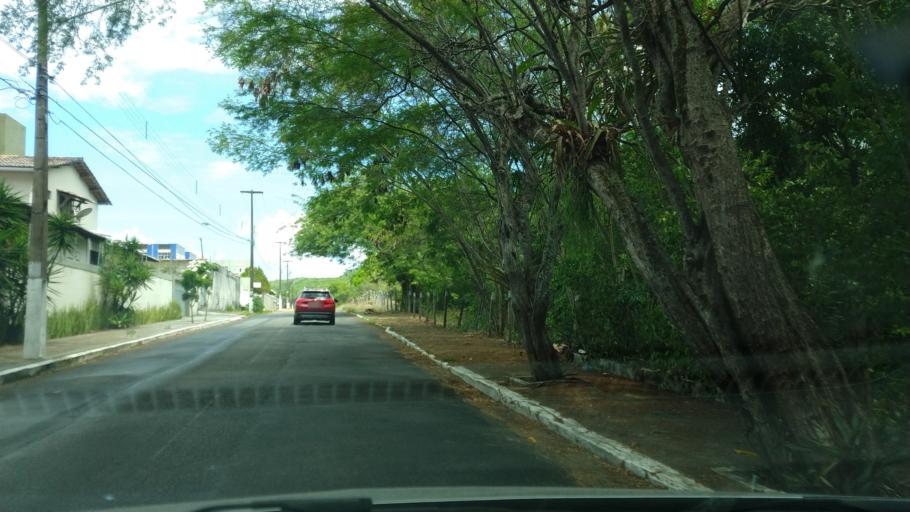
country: BR
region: Rio Grande do Norte
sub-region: Natal
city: Natal
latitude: -5.8467
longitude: -35.1969
